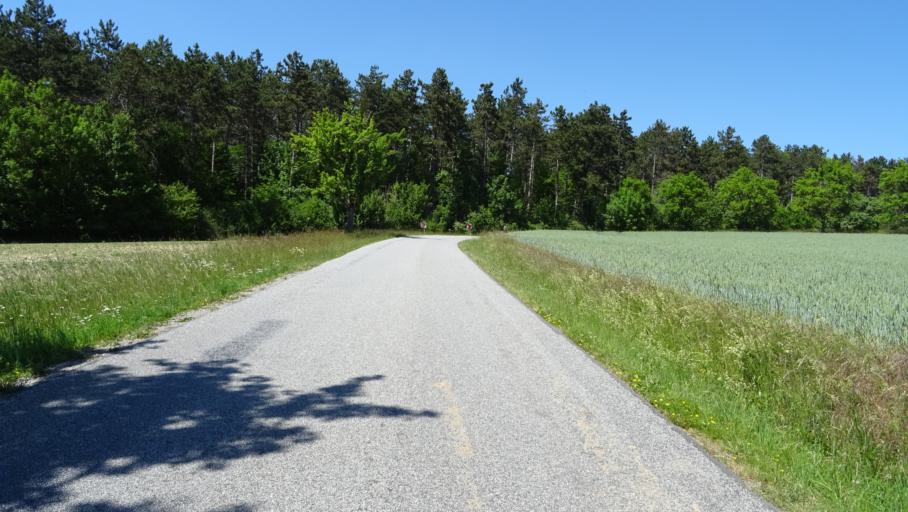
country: DE
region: Baden-Wuerttemberg
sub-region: Karlsruhe Region
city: Seckach
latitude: 49.4734
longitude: 9.3218
